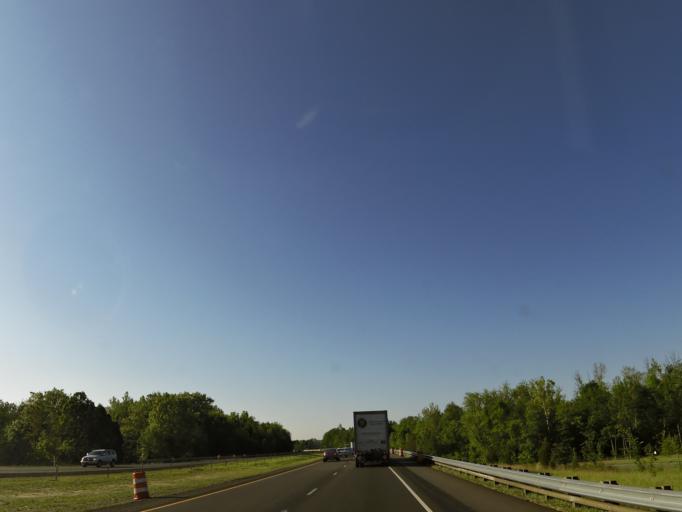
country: US
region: Indiana
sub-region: Jackson County
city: Seymour
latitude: 38.9187
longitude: -85.8356
